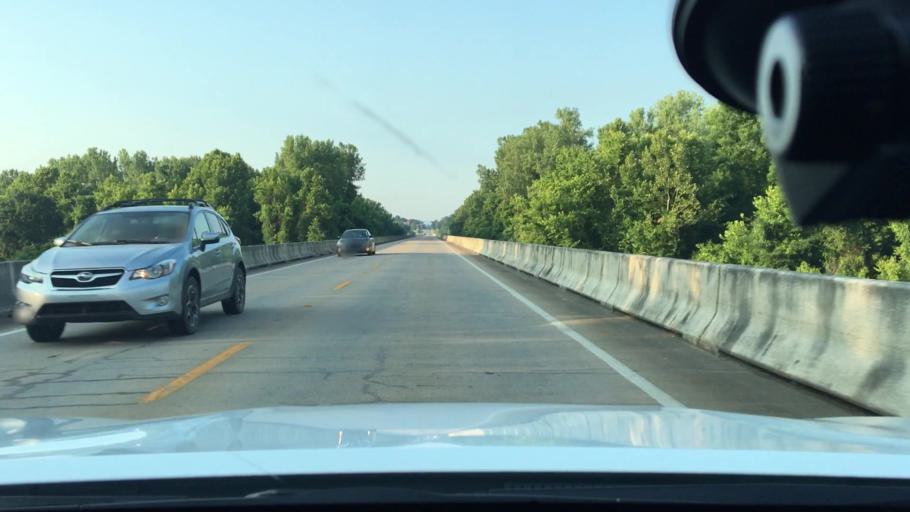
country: US
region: Arkansas
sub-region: Johnson County
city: Clarksville
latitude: 35.3999
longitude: -93.5311
